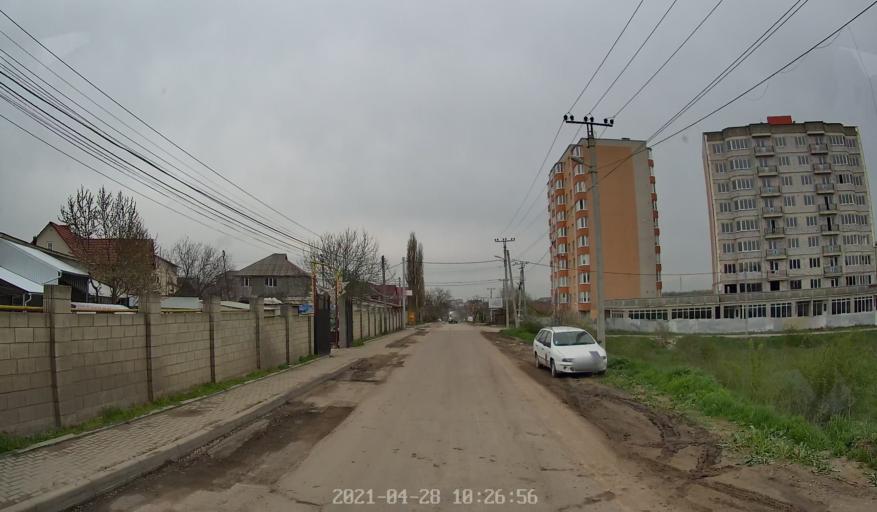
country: MD
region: Chisinau
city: Chisinau
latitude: 46.9935
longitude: 28.9348
